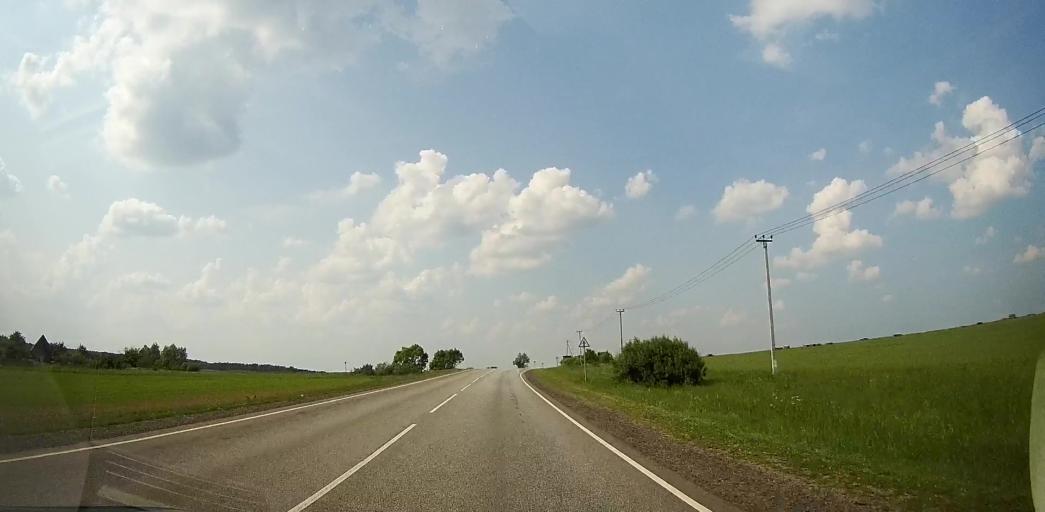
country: RU
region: Moskovskaya
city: Malino
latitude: 55.0332
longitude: 38.1595
